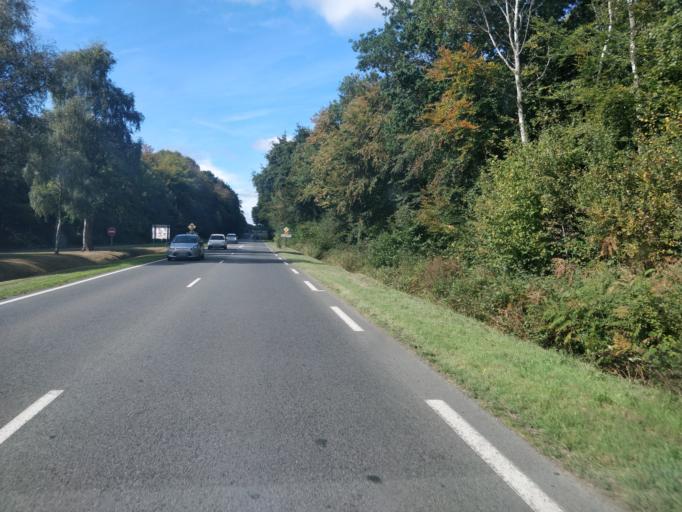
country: FR
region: Brittany
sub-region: Departement des Cotes-d'Armor
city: Erquy
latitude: 48.5954
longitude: -2.4795
